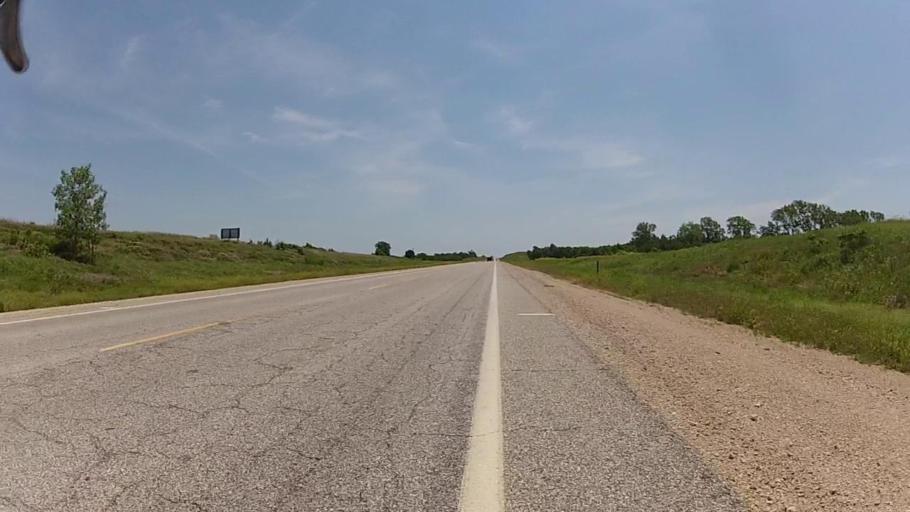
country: US
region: Kansas
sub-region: Chautauqua County
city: Sedan
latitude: 37.1132
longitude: -96.4527
